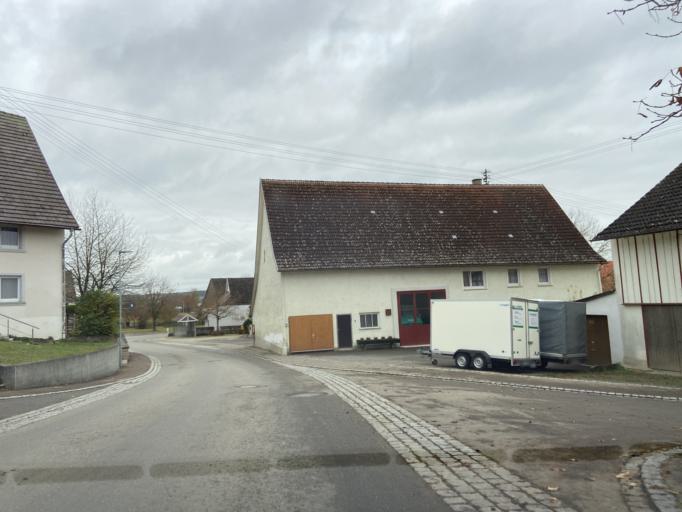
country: DE
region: Baden-Wuerttemberg
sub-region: Tuebingen Region
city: Messkirch
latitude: 48.0084
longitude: 9.1598
